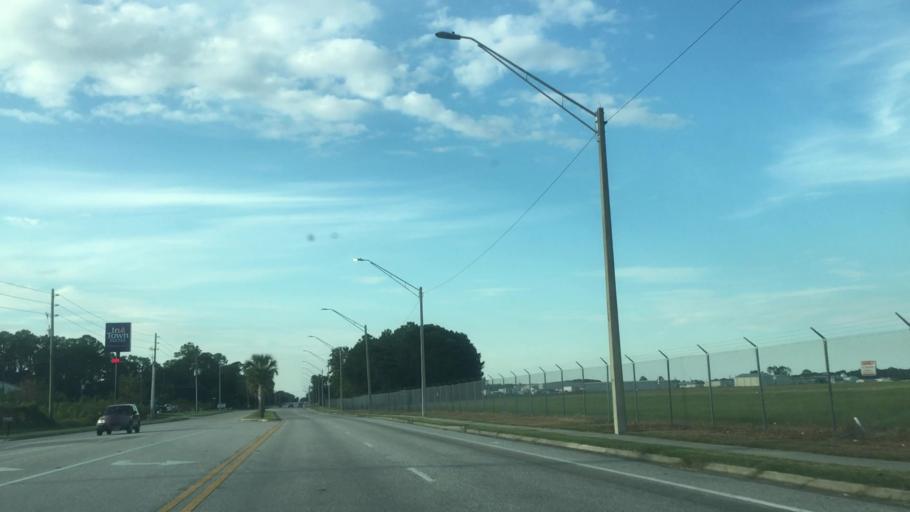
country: US
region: Florida
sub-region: Duval County
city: Atlantic Beach
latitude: 30.3253
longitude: -81.5231
